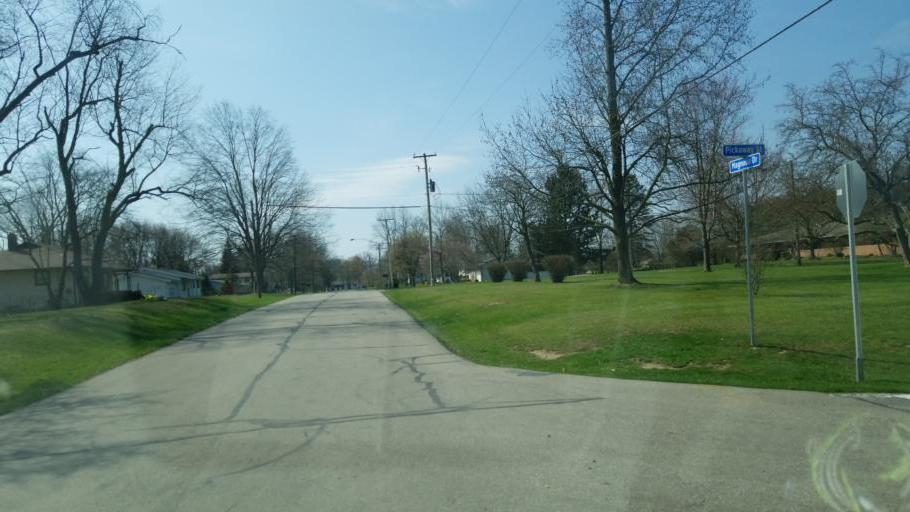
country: US
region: Ohio
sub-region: Delaware County
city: Delaware
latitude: 40.2845
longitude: -83.0739
